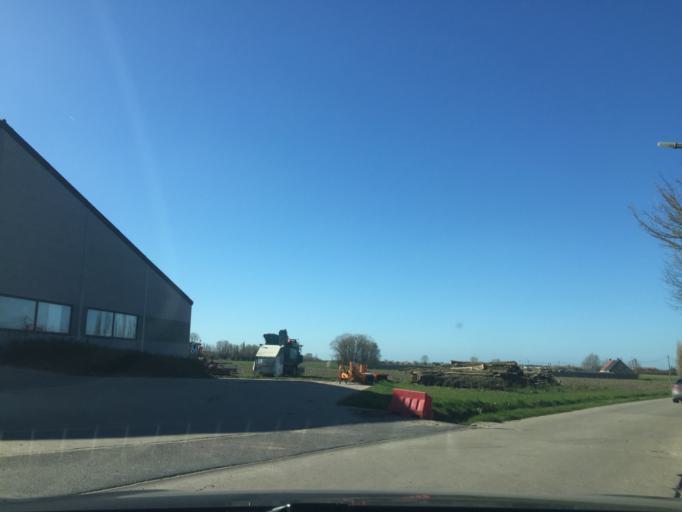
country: BE
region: Flanders
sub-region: Provincie West-Vlaanderen
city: Hooglede
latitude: 50.9874
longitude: 3.0794
